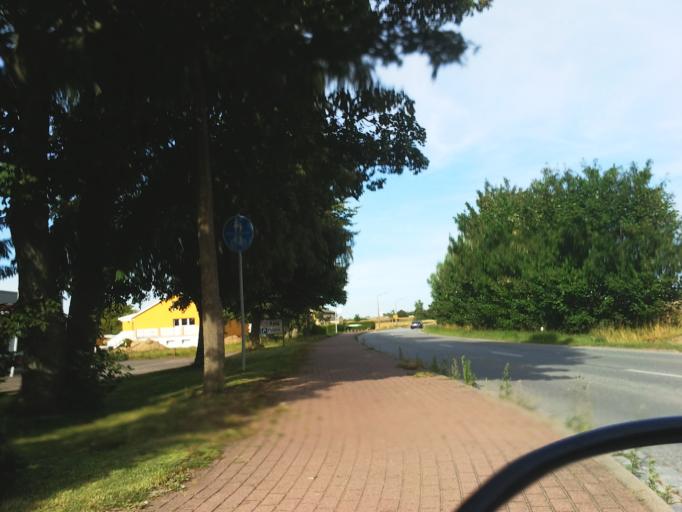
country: DE
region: Mecklenburg-Vorpommern
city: Stabelow
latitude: 54.0422
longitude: 12.0242
